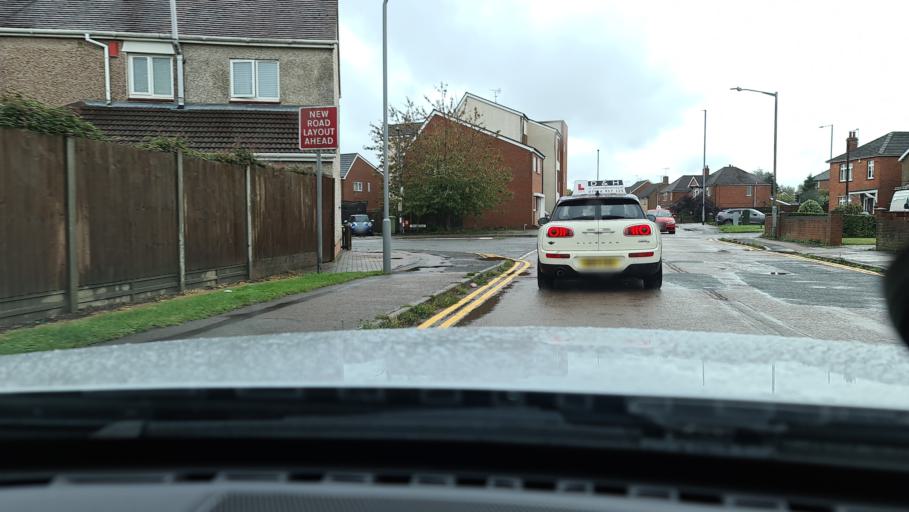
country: GB
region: England
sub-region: Buckinghamshire
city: Bletchley
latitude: 51.9981
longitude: -0.7290
